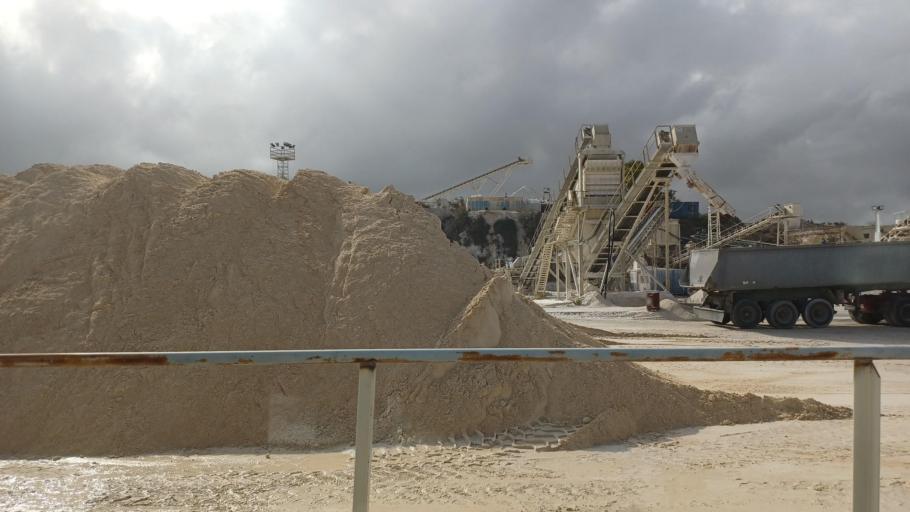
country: CY
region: Pafos
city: Polis
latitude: 35.0001
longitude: 32.3945
